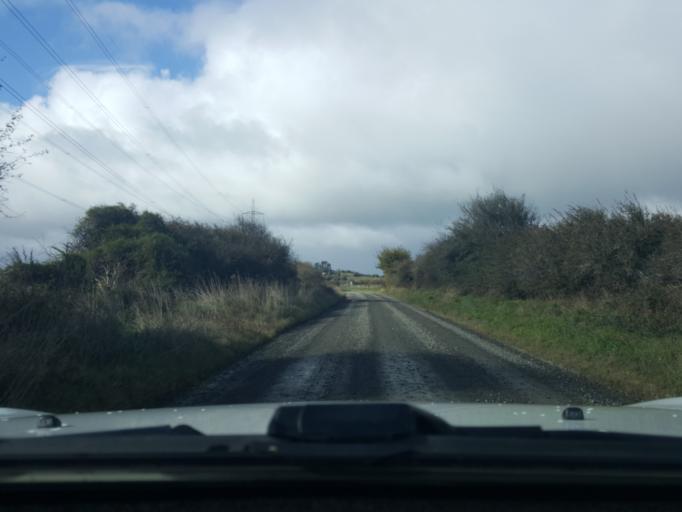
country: NZ
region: Waikato
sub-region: Waikato District
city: Te Kauwhata
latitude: -37.4164
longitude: 175.0663
